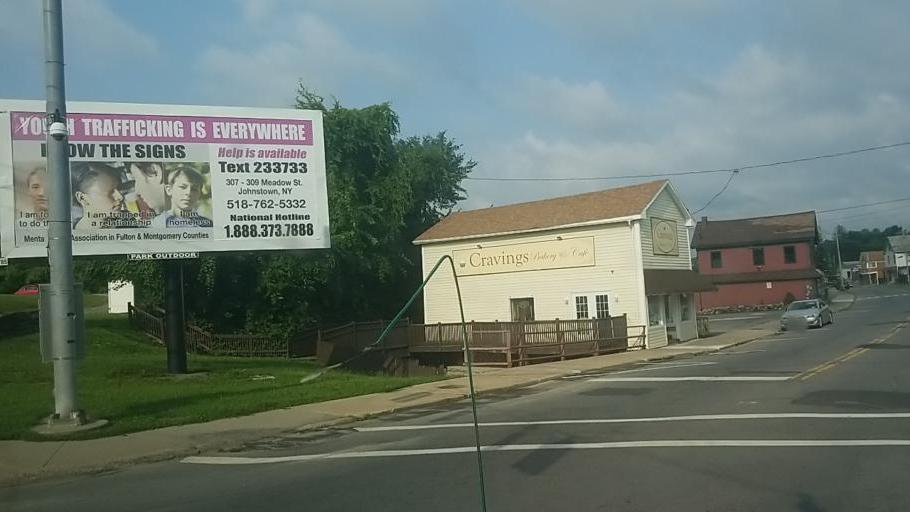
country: US
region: New York
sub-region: Fulton County
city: Gloversville
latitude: 43.0504
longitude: -74.3489
